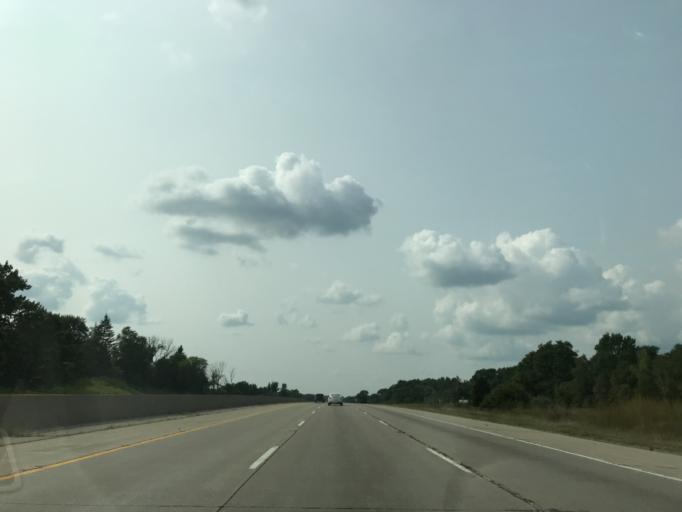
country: US
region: Michigan
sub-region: Livingston County
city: Brighton
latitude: 42.5575
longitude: -83.8223
